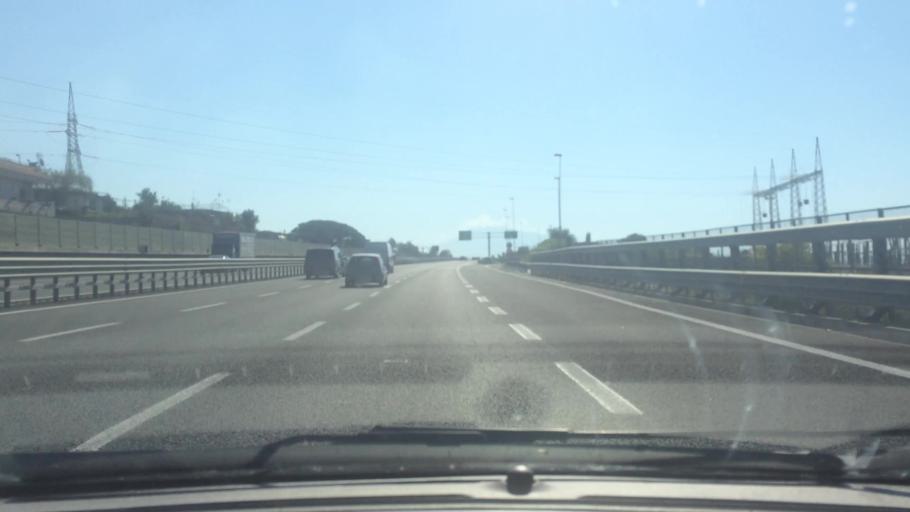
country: IT
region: Campania
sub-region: Provincia di Napoli
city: Ercolano
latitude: 40.8095
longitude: 14.3625
